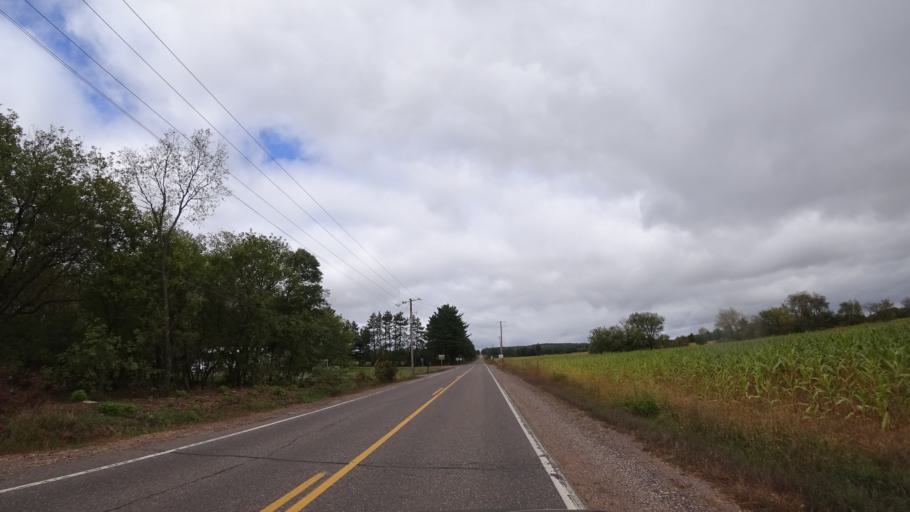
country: US
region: Wisconsin
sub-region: Chippewa County
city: Lake Wissota
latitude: 44.9794
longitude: -91.2677
